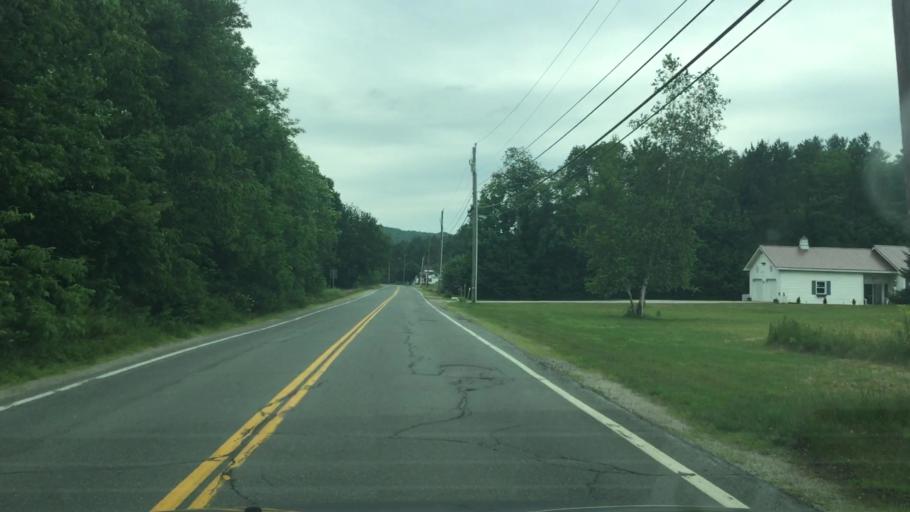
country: US
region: New Hampshire
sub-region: Grafton County
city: Littleton
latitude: 44.2350
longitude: -71.7576
